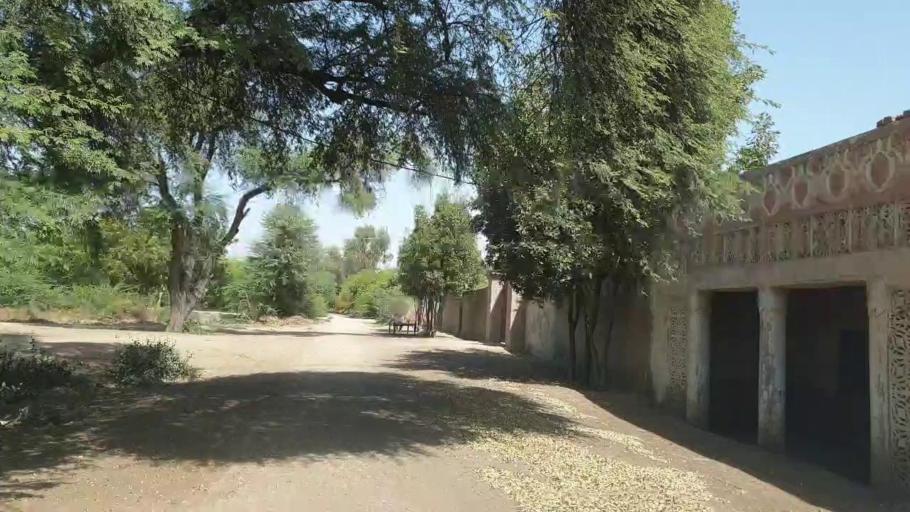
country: PK
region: Sindh
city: Naukot
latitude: 24.9738
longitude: 69.4921
